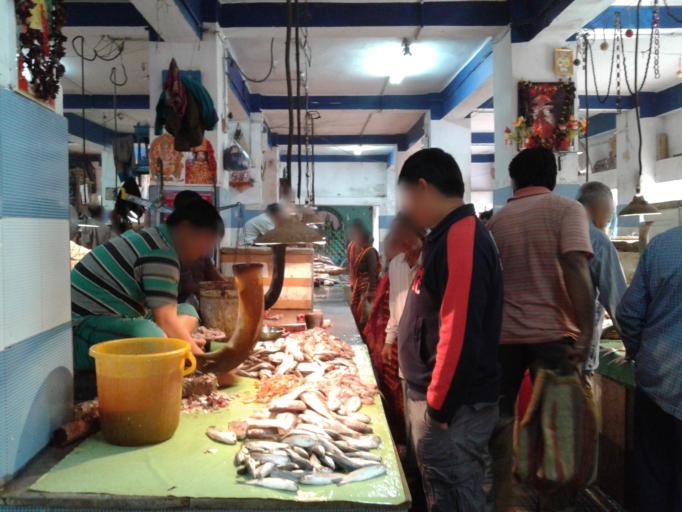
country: IN
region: West Bengal
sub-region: Kolkata
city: Kolkata
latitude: 22.5052
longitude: 88.3842
